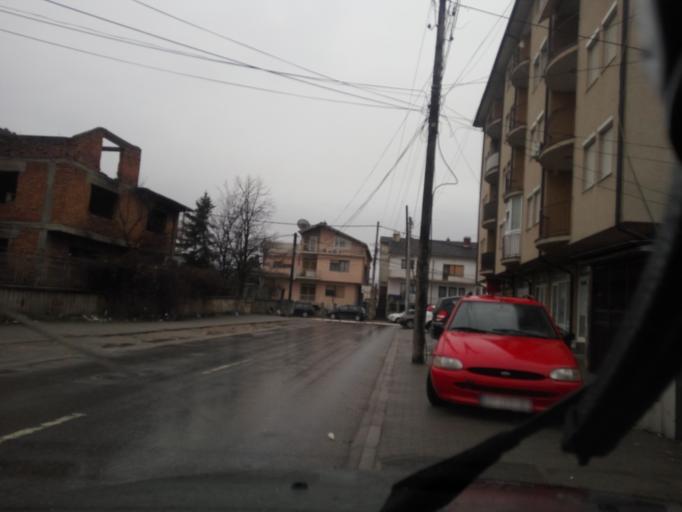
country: XK
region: Gjakova
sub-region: Komuna e Gjakoves
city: Gjakove
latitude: 42.3714
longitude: 20.4404
